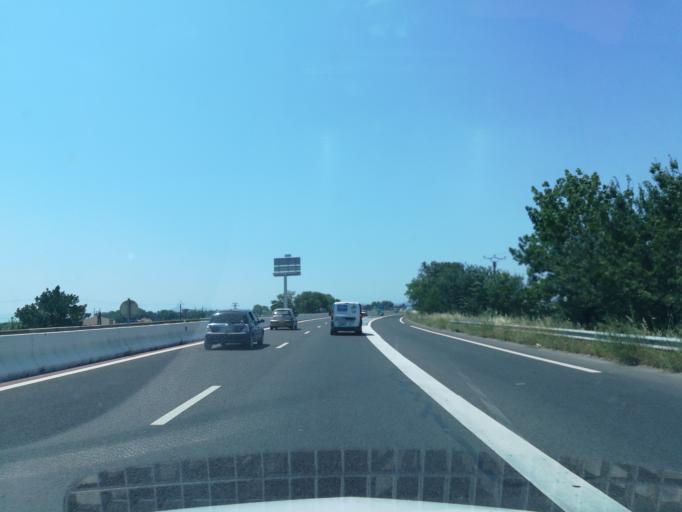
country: FR
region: Languedoc-Roussillon
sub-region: Departement des Pyrenees-Orientales
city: Perpignan
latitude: 42.7087
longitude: 2.8781
